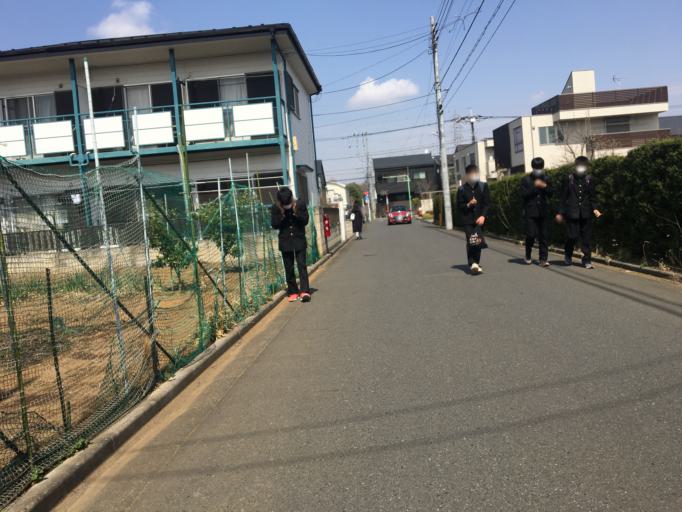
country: JP
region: Tokyo
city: Mitaka-shi
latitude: 35.6842
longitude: 139.5440
